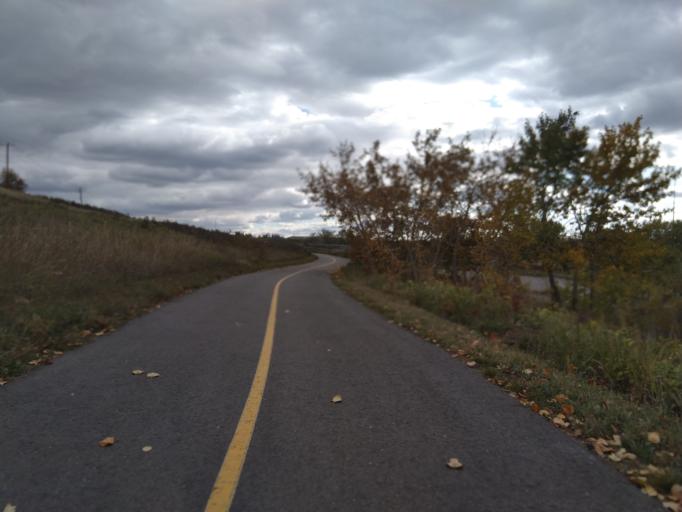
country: CA
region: Alberta
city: Calgary
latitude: 51.0392
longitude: -114.0026
